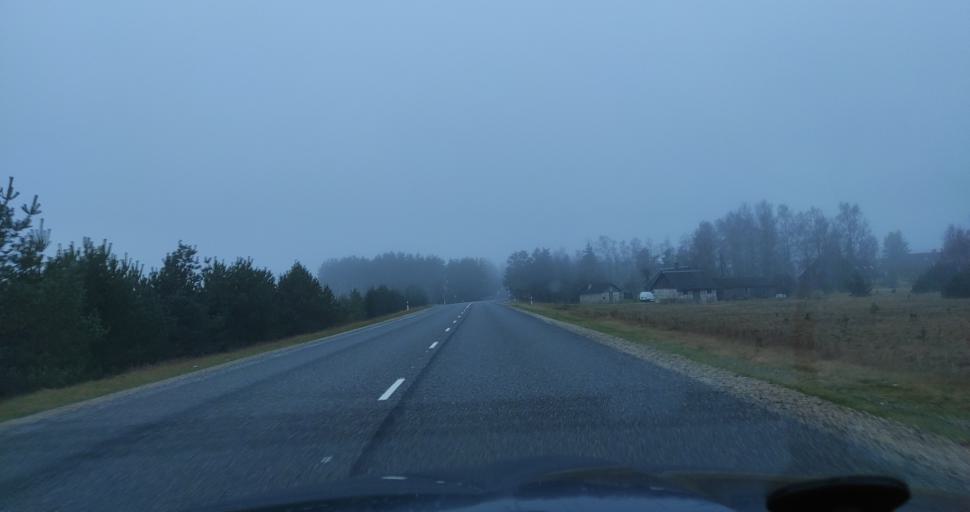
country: LV
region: Alsunga
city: Alsunga
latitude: 57.0089
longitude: 21.3888
